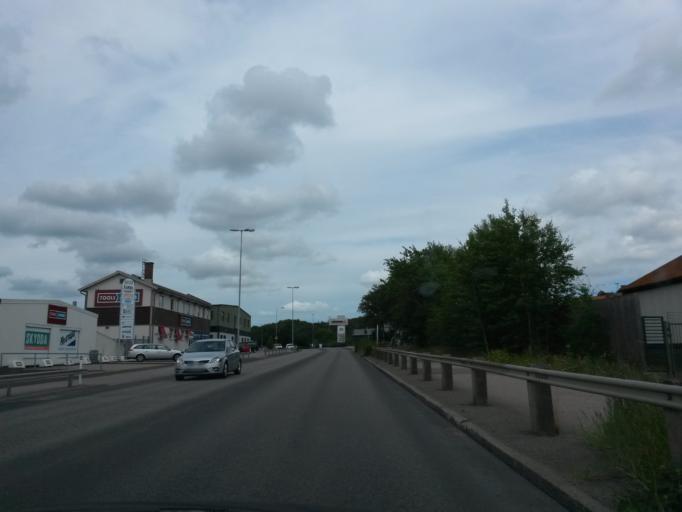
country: SE
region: Halland
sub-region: Varbergs Kommun
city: Varberg
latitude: 57.1183
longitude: 12.2586
